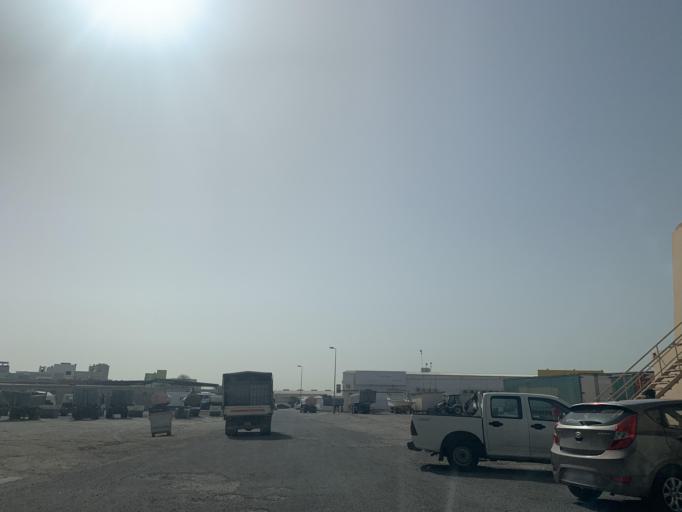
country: BH
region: Northern
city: Sitrah
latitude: 26.1560
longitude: 50.6111
